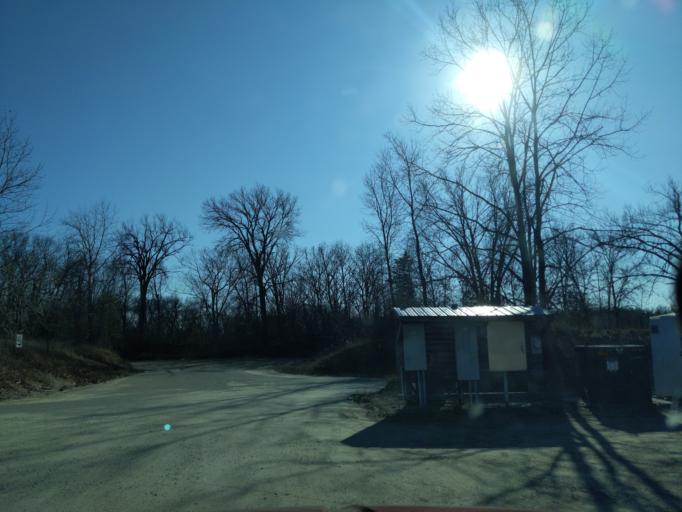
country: US
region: Wisconsin
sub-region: Waushara County
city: Wautoma
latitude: 44.1169
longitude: -89.2814
